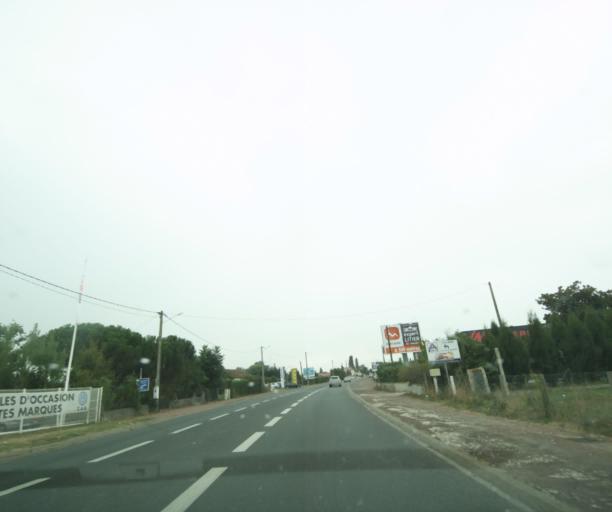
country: FR
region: Poitou-Charentes
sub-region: Departement de la Charente-Maritime
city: Breuil-Magne
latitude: 45.9533
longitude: -0.9377
